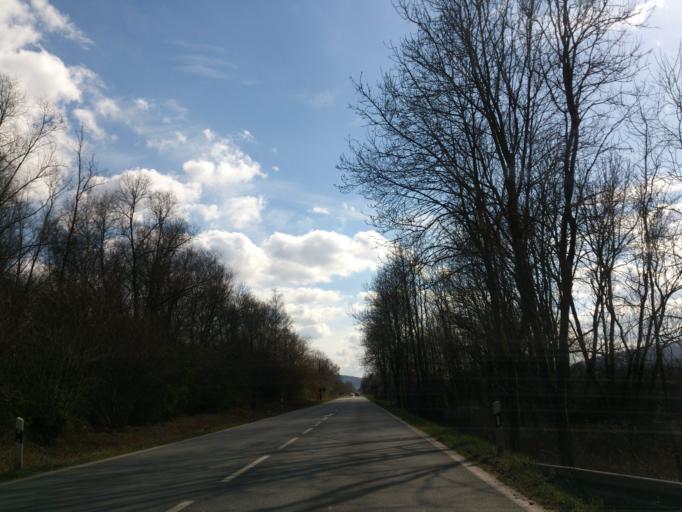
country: DE
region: Lower Saxony
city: Boffzen
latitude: 51.7571
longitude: 9.3732
